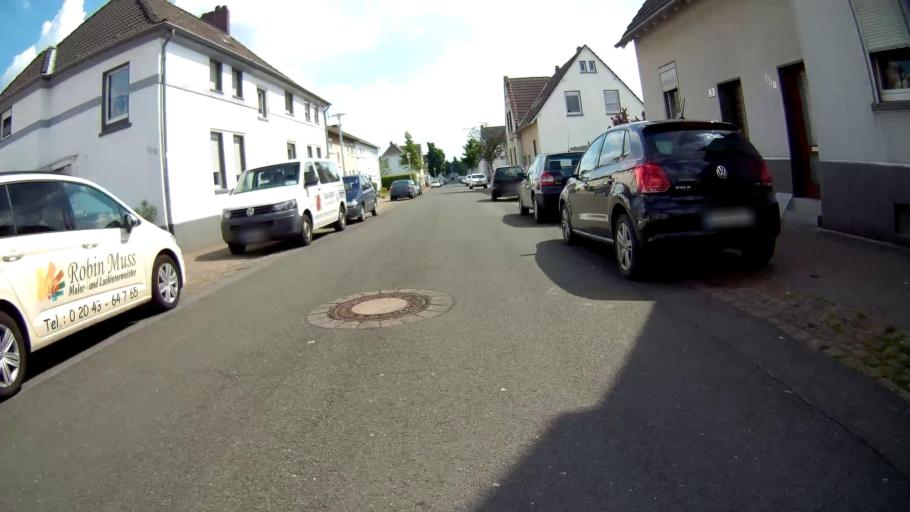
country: DE
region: North Rhine-Westphalia
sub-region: Regierungsbezirk Munster
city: Gladbeck
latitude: 51.5875
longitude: 6.9798
